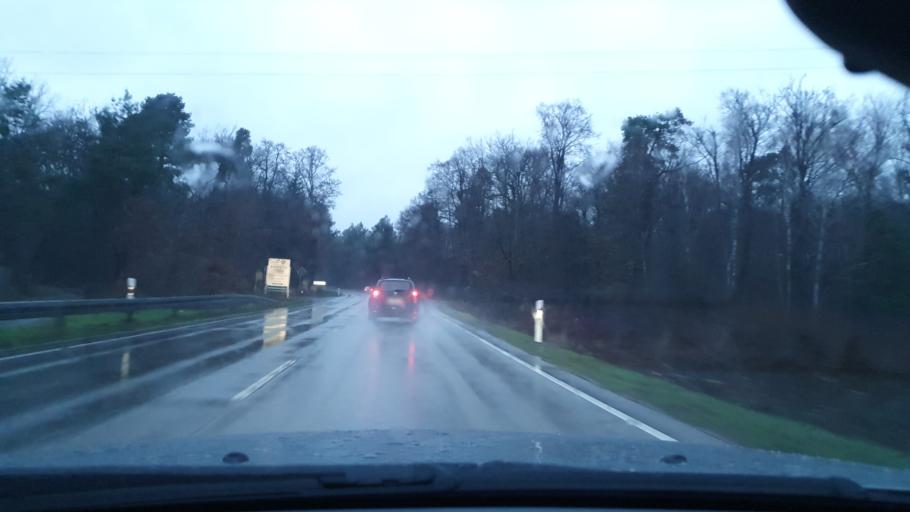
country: DE
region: Rheinland-Pfalz
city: Bechhofen
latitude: 49.3650
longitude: 7.3798
